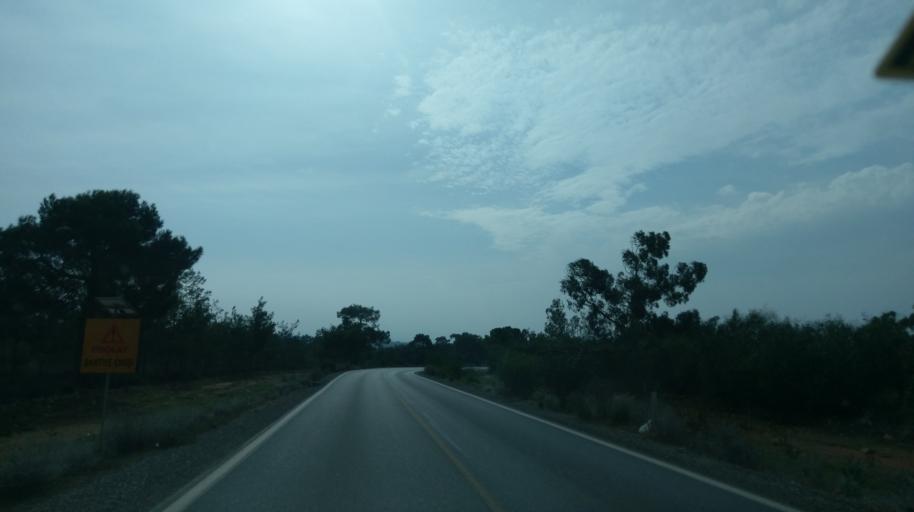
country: CY
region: Lefkosia
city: Morfou
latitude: 35.2744
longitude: 33.0413
